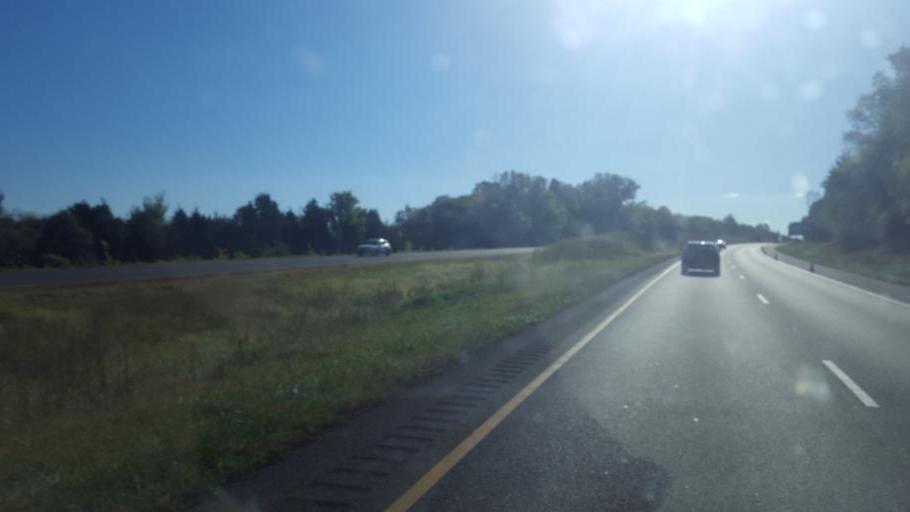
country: US
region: Maryland
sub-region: Washington County
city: Wilson-Conococheague
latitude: 39.6367
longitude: -77.8206
